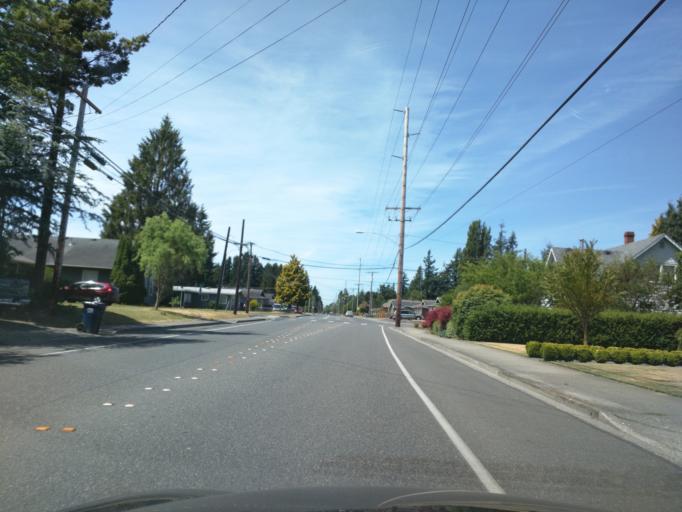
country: US
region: Washington
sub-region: Whatcom County
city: Lynden
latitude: 48.9466
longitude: -122.4625
